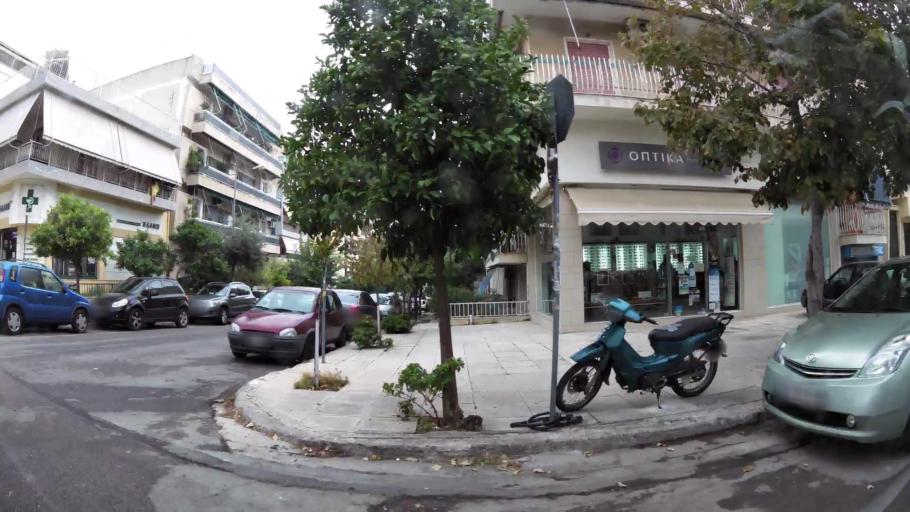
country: GR
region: Attica
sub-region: Nomarchia Athinas
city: Kaisariani
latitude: 37.9557
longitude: 23.7624
